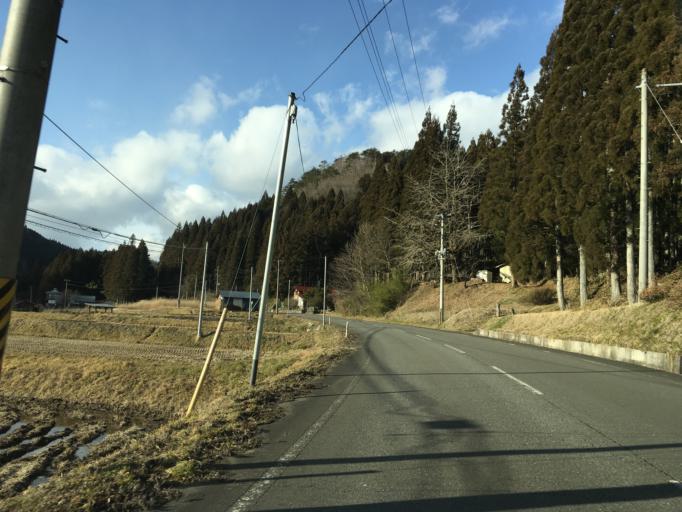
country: JP
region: Miyagi
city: Furukawa
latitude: 38.8011
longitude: 140.8347
